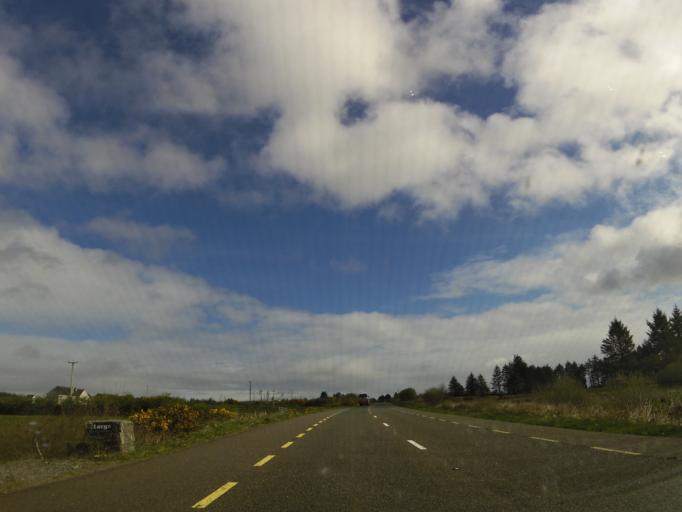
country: IE
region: Connaught
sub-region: Maigh Eo
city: Ballyhaunis
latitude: 53.9016
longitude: -8.7979
